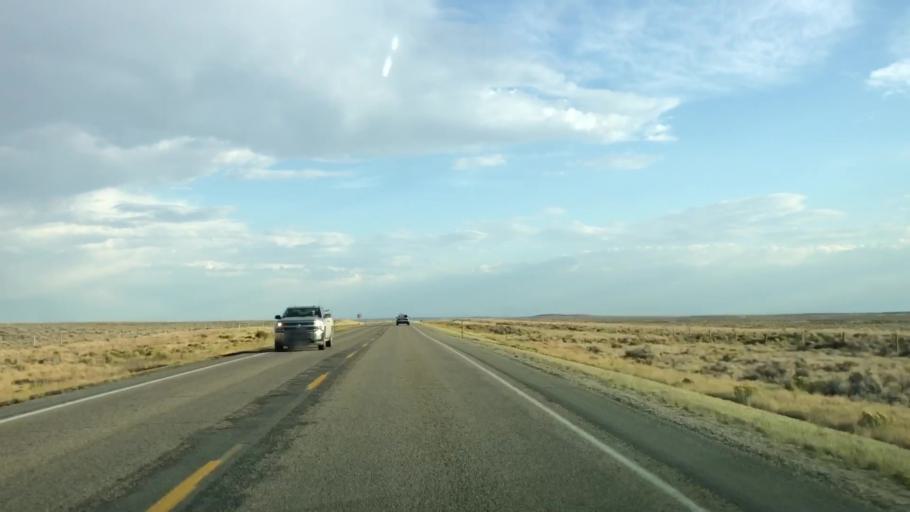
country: US
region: Wyoming
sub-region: Sublette County
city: Pinedale
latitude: 42.4092
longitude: -109.5515
